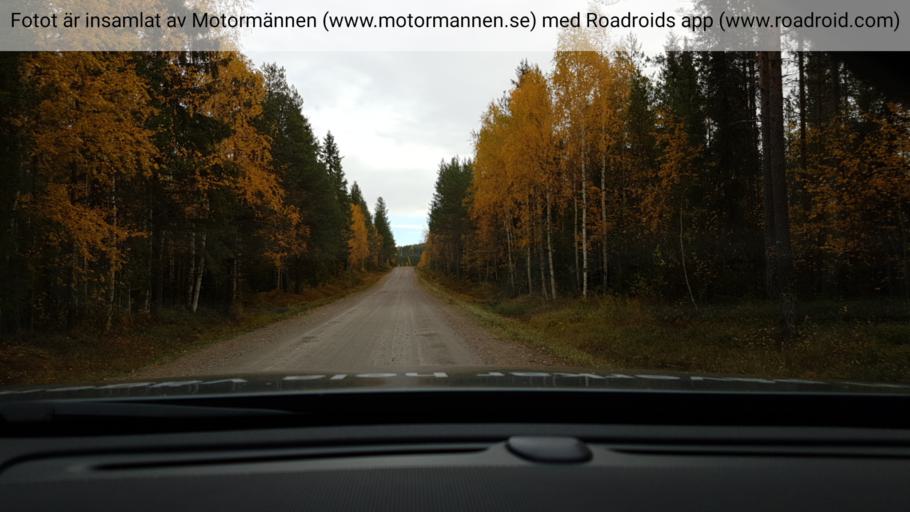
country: SE
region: Norrbotten
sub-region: Overkalix Kommun
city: OEverkalix
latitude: 66.2912
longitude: 22.9562
